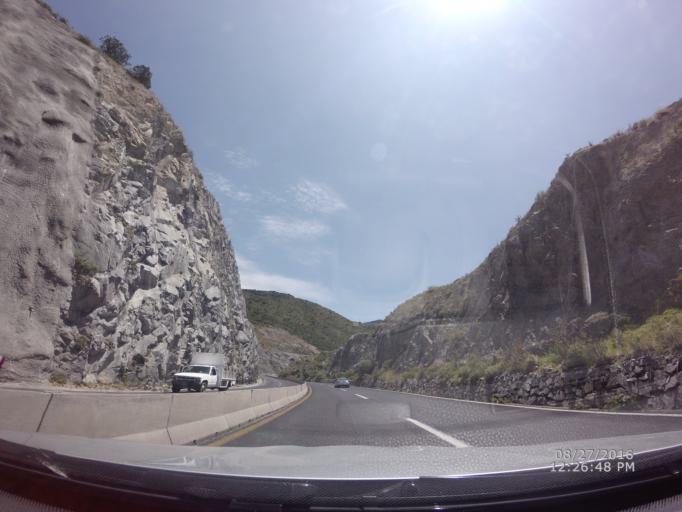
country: MX
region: Hidalgo
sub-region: Mineral de la Reforma
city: Colonia Militar
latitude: 20.1269
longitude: -98.6970
